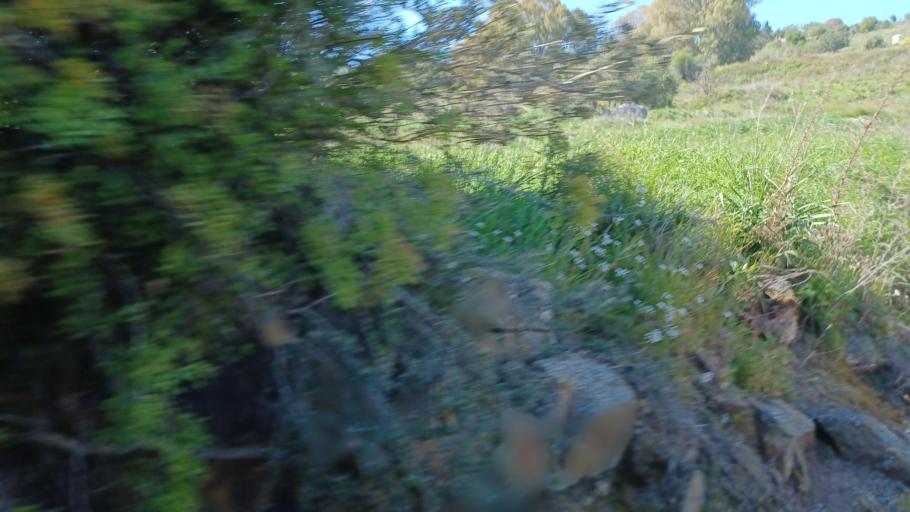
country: CY
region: Pafos
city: Polis
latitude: 34.9693
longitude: 32.3973
